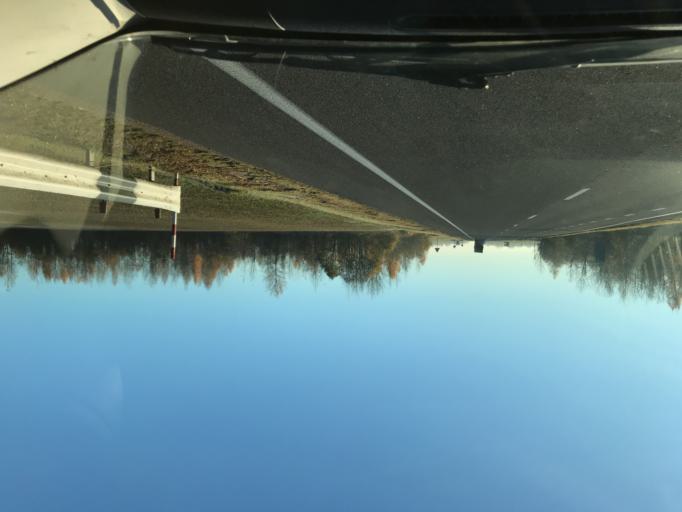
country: BY
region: Vitebsk
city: Vitebsk
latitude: 55.0031
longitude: 30.3355
